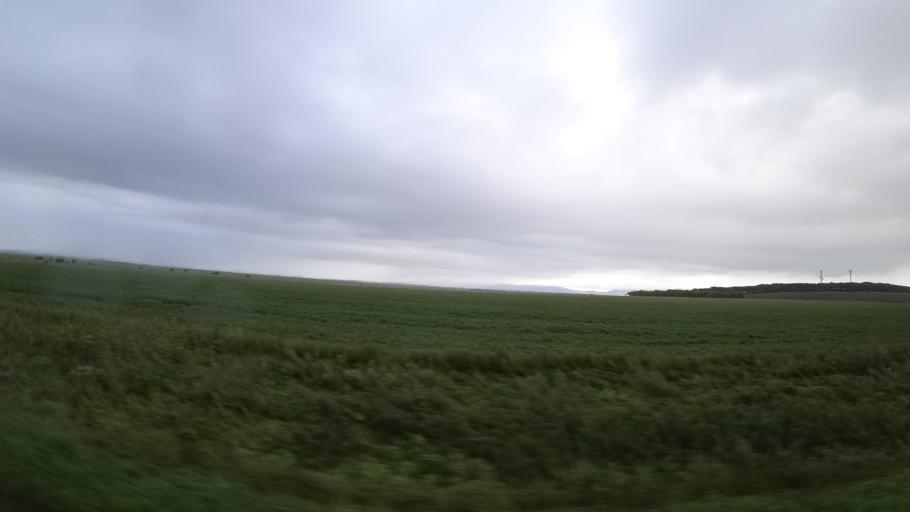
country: RU
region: Primorskiy
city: Chernigovka
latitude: 44.3756
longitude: 132.5297
